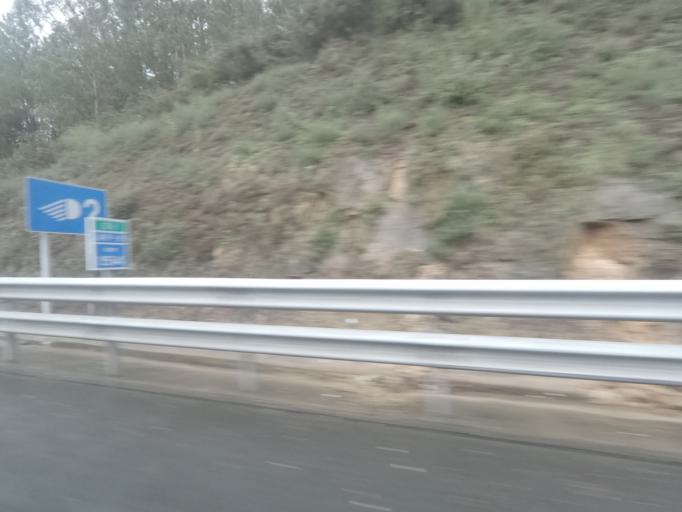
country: ES
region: Galicia
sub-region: Provincia de Pontevedra
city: Vigo
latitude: 42.2349
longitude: -8.6799
